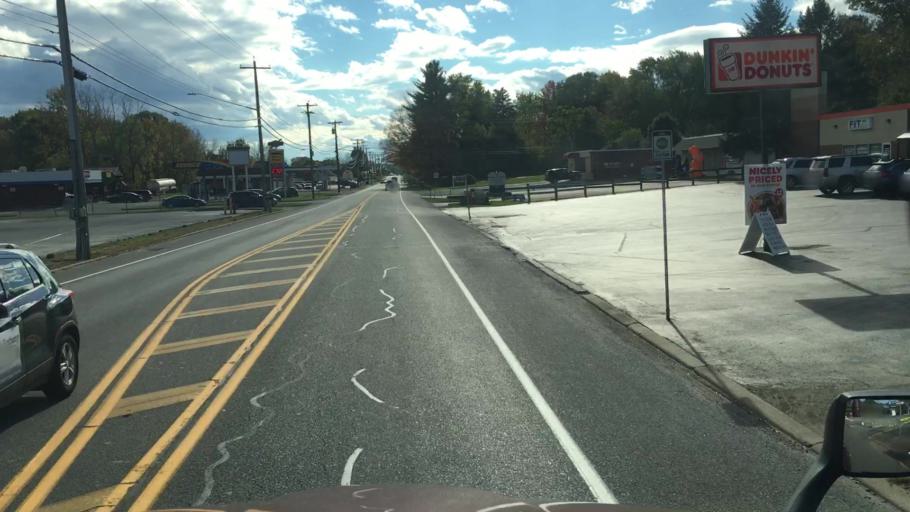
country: US
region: New York
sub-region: Schenectady County
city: East Glenville
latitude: 42.9098
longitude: -73.8988
